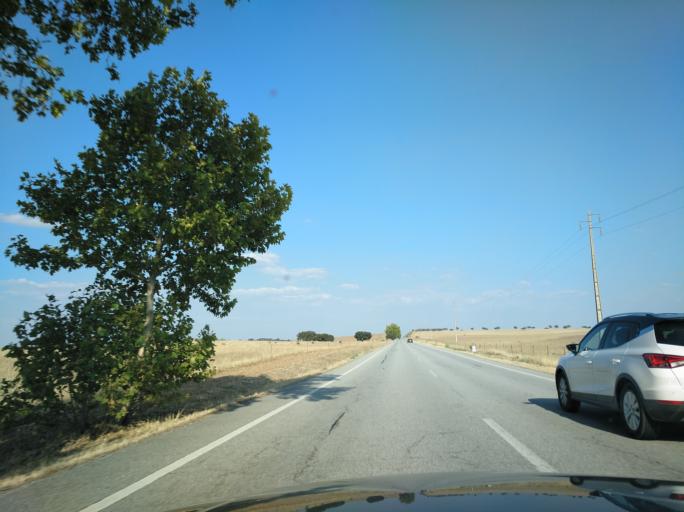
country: PT
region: Evora
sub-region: Mourao
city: Mourao
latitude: 38.3815
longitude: -7.2928
